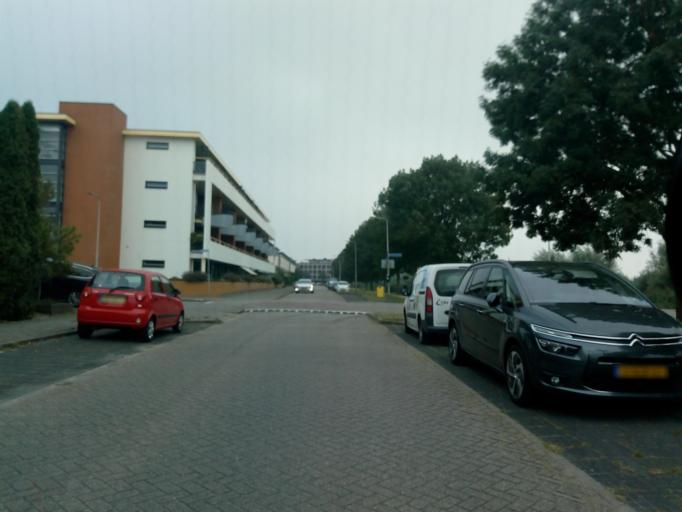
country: NL
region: South Holland
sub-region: Gemeente Alphen aan den Rijn
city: Alphen aan den Rijn
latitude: 52.1170
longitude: 4.6555
